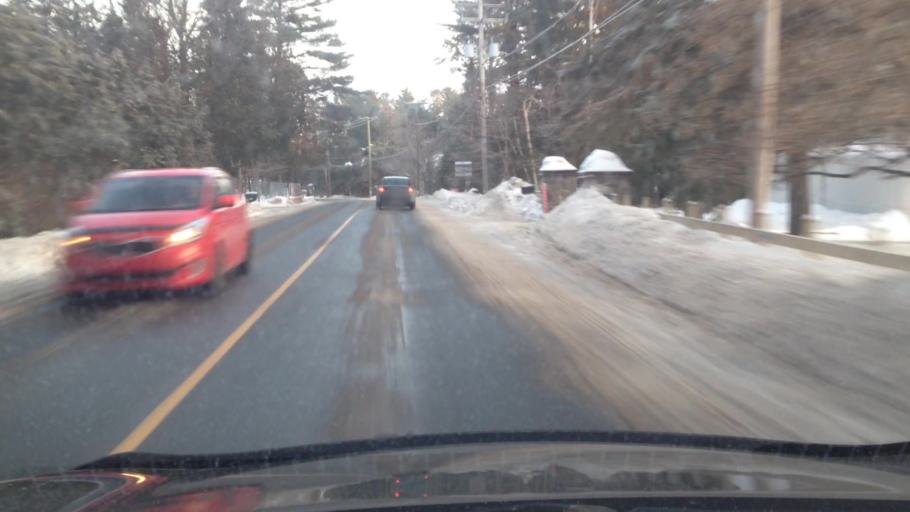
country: CA
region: Quebec
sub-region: Lanaudiere
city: Sainte-Julienne
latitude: 45.9528
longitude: -73.7533
